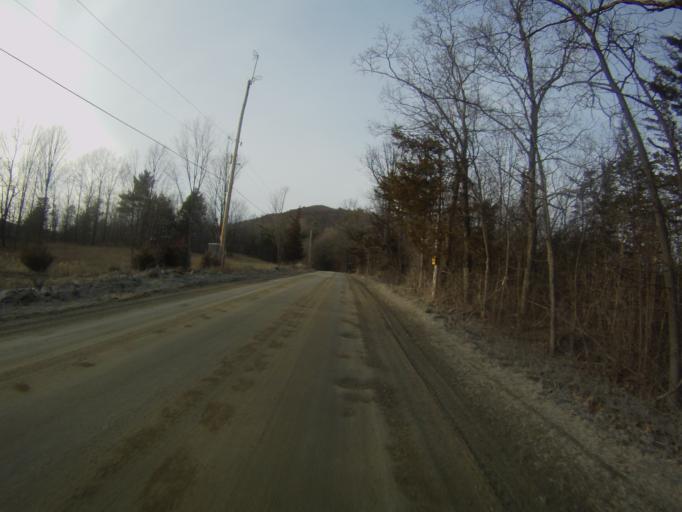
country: US
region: Vermont
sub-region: Addison County
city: Middlebury (village)
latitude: 44.0291
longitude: -73.2608
